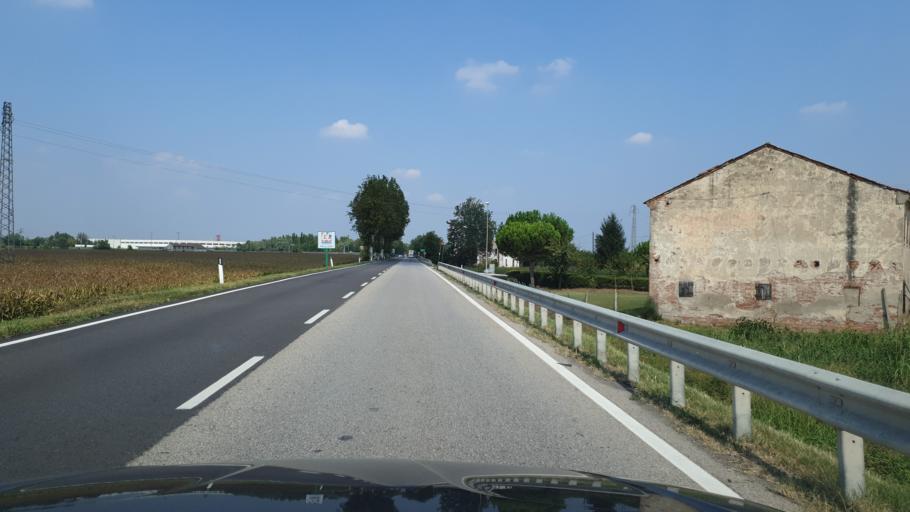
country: IT
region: Veneto
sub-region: Provincia di Rovigo
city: Bosaro
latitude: 45.0192
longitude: 11.7711
